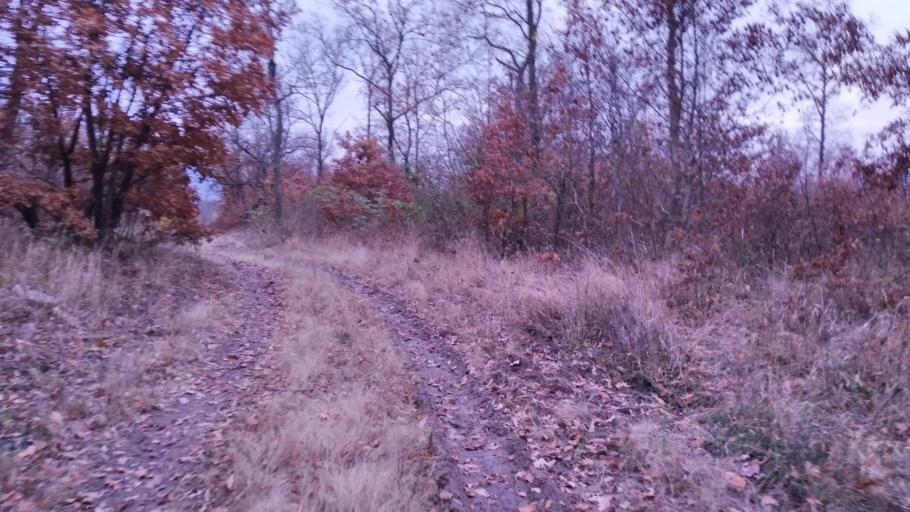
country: HU
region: Pest
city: Csobanka
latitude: 47.6707
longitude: 18.9592
